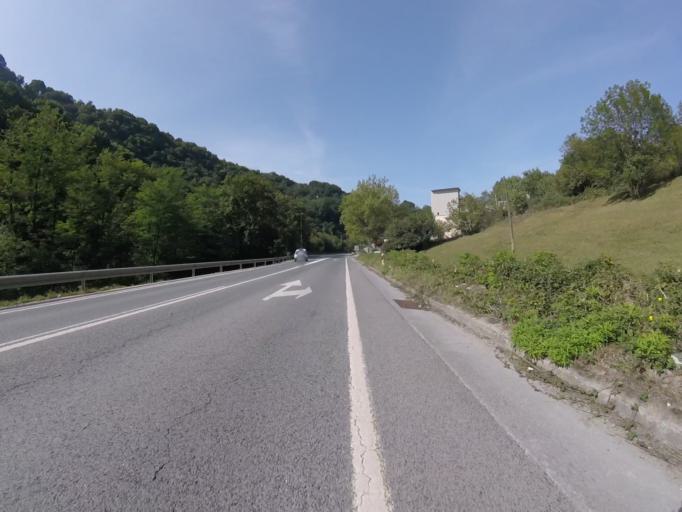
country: ES
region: Navarre
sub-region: Provincia de Navarra
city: Doneztebe
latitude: 43.1412
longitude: -1.5906
